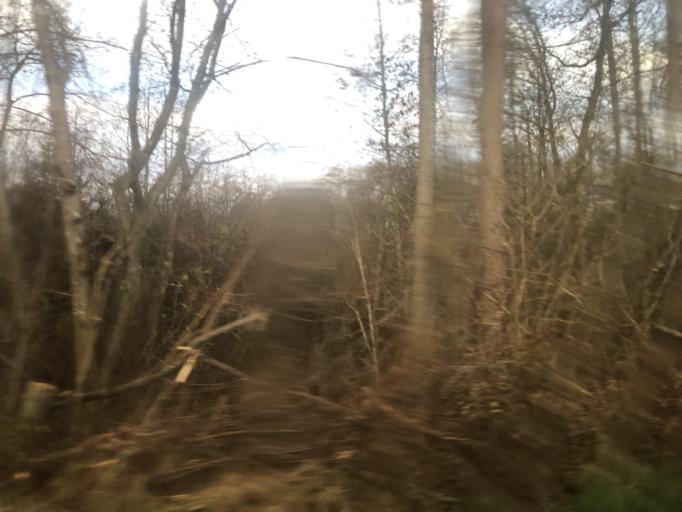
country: SE
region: Skane
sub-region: Lunds Kommun
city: Veberod
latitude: 55.6052
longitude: 13.5366
